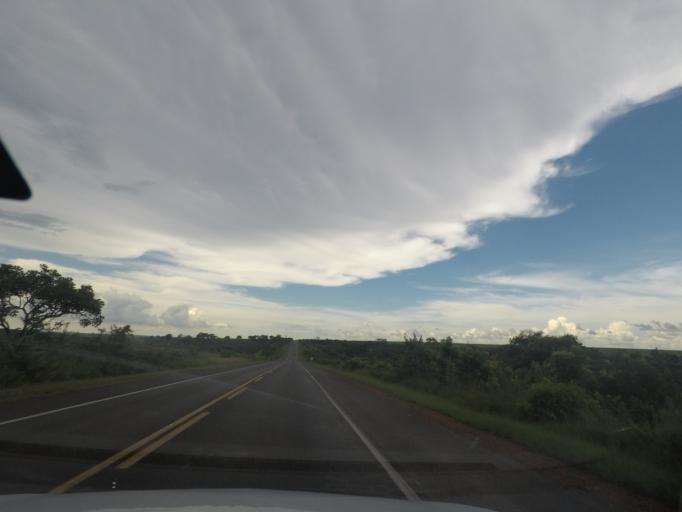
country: BR
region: Minas Gerais
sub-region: Prata
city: Prata
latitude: -19.5921
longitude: -48.8307
